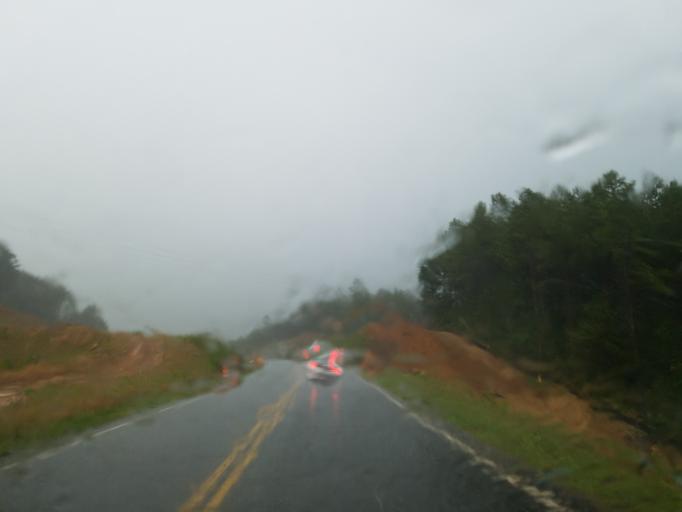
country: US
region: Georgia
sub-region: Bartow County
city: Adairsville
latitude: 34.3731
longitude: -84.9613
